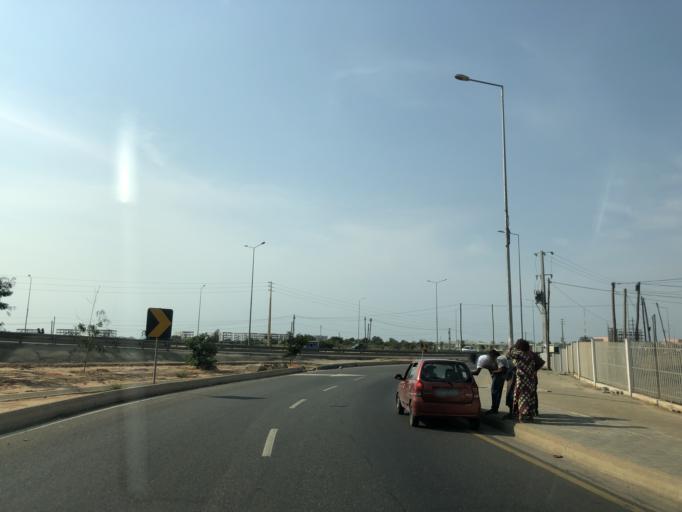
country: AO
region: Luanda
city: Luanda
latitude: -8.9716
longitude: 13.2550
